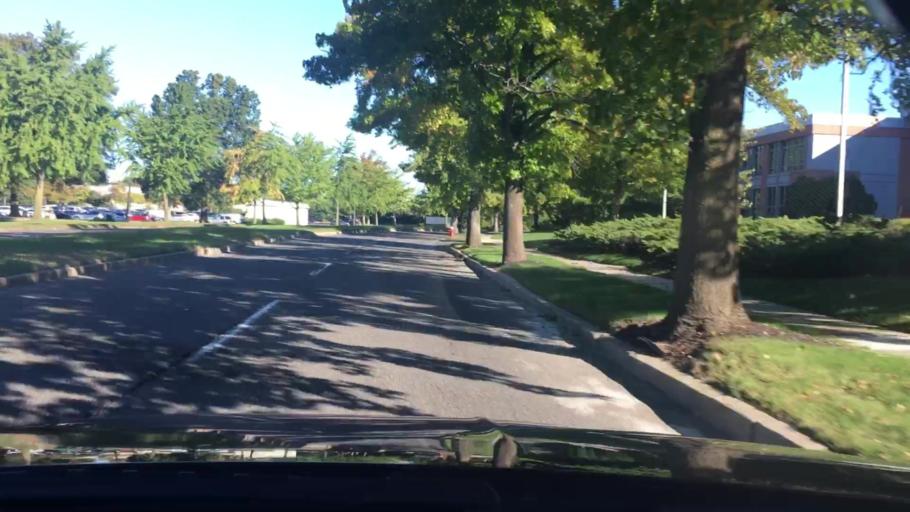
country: US
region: New York
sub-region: Suffolk County
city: Melville
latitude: 40.7725
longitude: -73.4134
